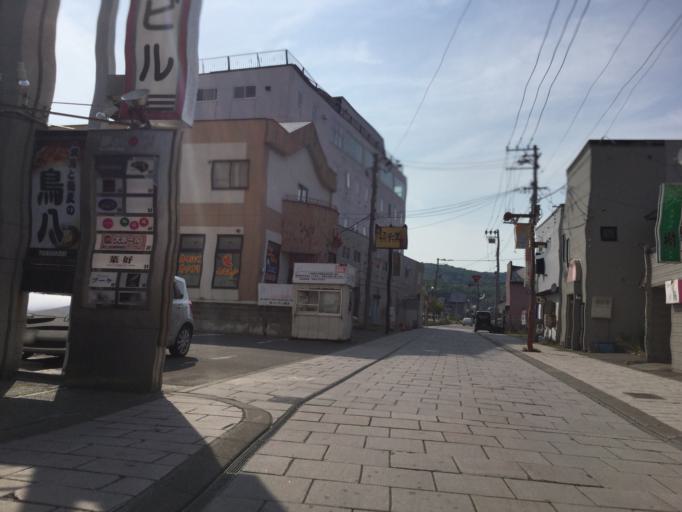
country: JP
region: Hokkaido
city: Wakkanai
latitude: 45.3981
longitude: 141.6847
